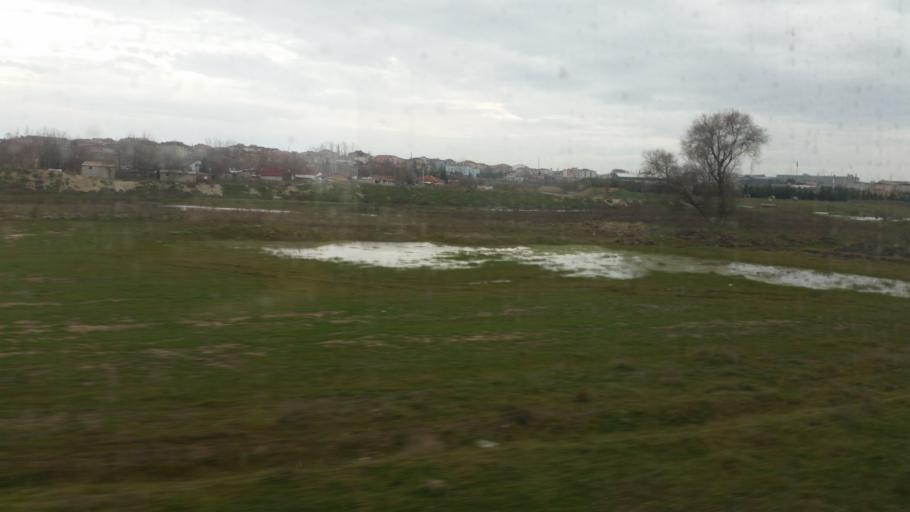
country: TR
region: Tekirdag
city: Marmaracik
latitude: 41.1749
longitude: 27.7688
